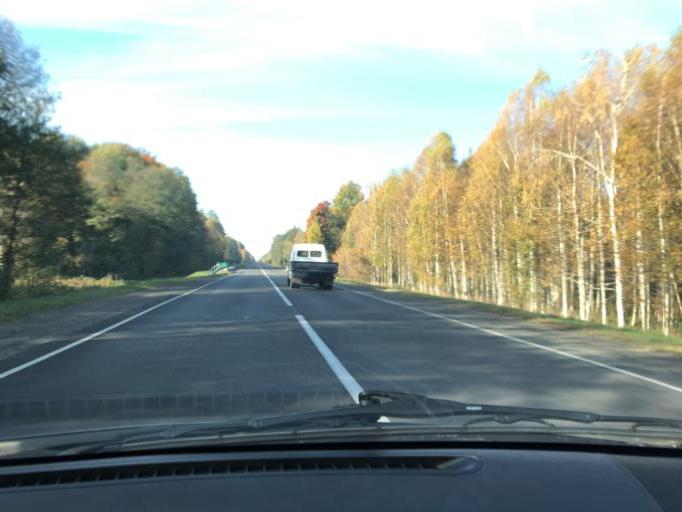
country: BY
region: Brest
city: Mikashevichy
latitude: 52.2422
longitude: 27.3285
